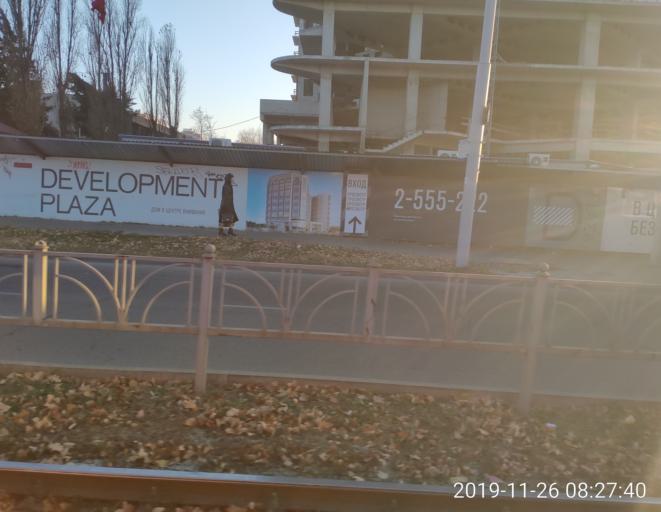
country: RU
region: Krasnodarskiy
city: Krasnodar
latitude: 45.0559
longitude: 39.0025
